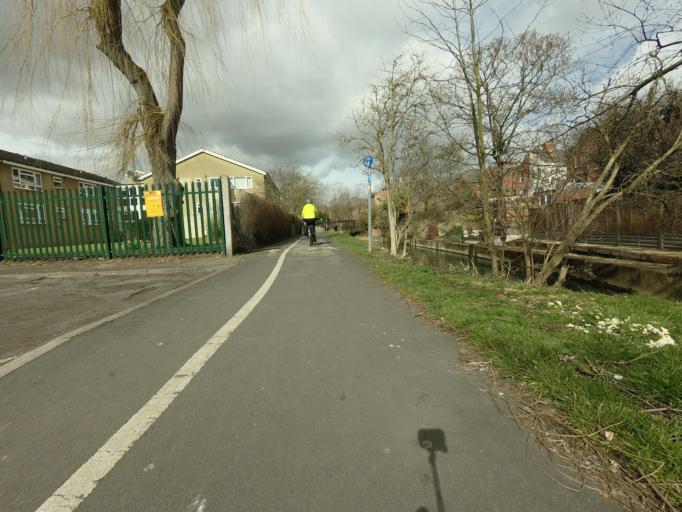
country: GB
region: England
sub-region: Lincolnshire
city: Grantham
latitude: 52.9092
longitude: -0.6357
